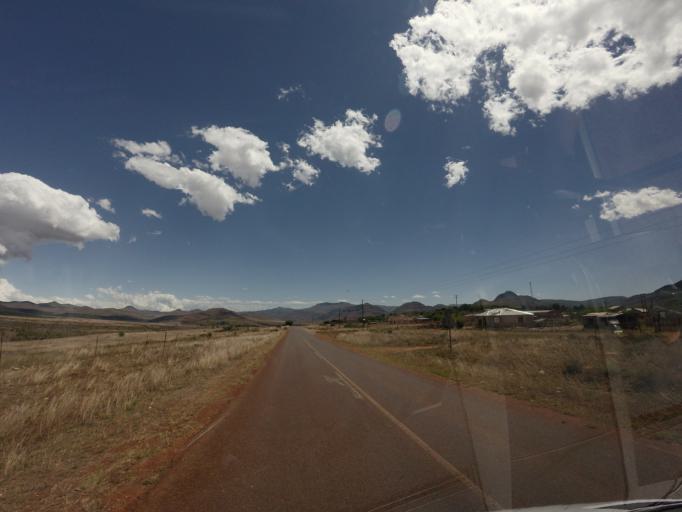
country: ZA
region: Mpumalanga
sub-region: Ehlanzeni District
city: Graksop
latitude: -24.6579
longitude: 30.8181
